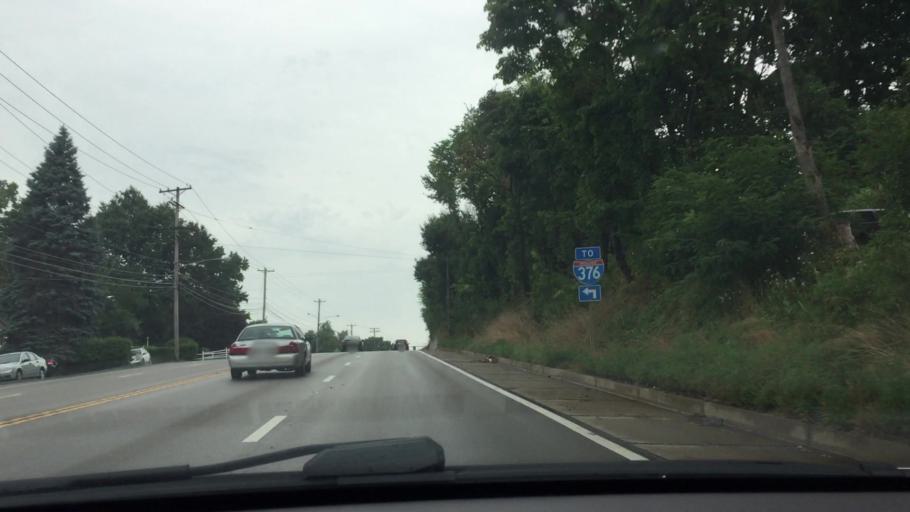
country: US
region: Pennsylvania
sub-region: Allegheny County
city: Carnegie
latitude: 40.3974
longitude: -80.0658
